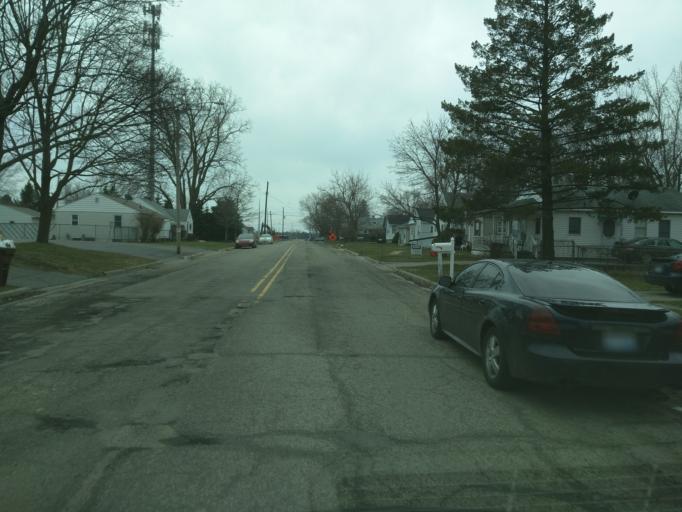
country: US
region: Michigan
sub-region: Ingham County
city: Edgemont Park
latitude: 42.7317
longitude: -84.5833
